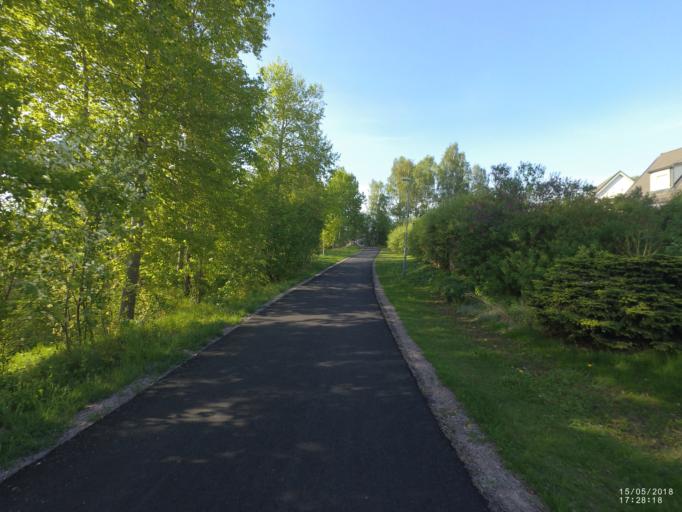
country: SE
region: Soedermanland
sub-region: Nykopings Kommun
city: Nykoping
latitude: 58.7269
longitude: 17.0242
